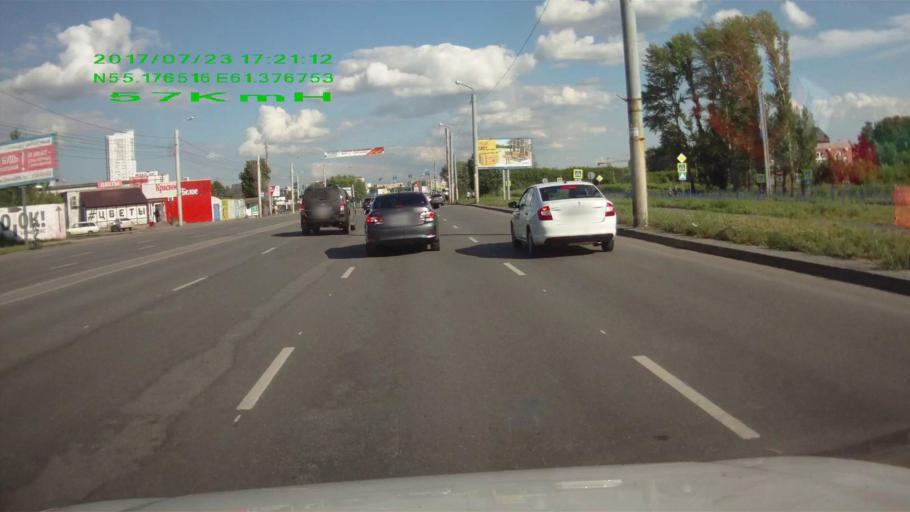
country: RU
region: Chelyabinsk
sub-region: Gorod Chelyabinsk
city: Chelyabinsk
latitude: 55.1762
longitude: 61.3775
